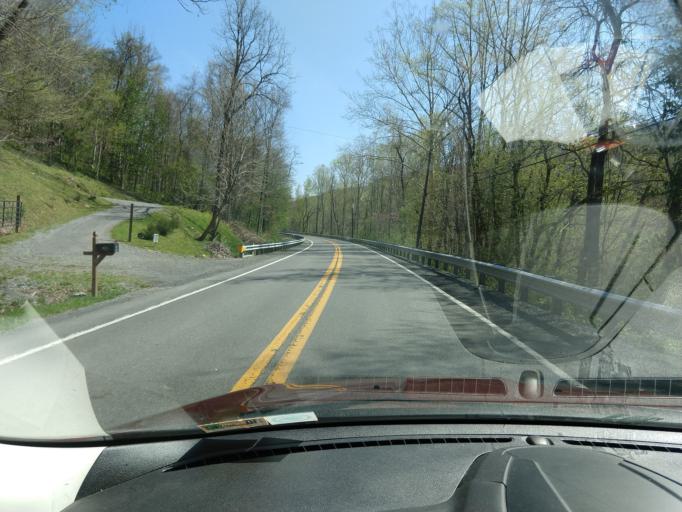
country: US
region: West Virginia
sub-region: Greenbrier County
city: Alderson
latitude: 37.7170
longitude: -80.6169
